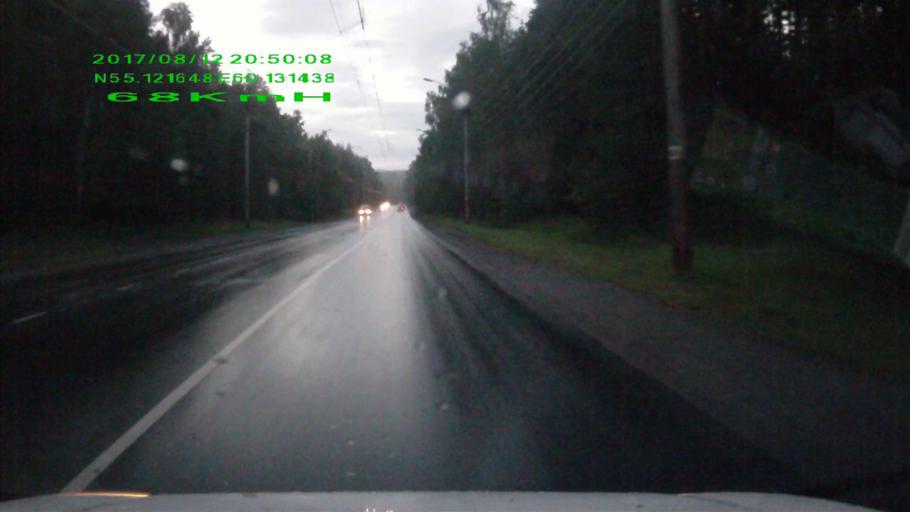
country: RU
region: Chelyabinsk
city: Turgoyak
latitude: 55.1217
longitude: 60.1315
